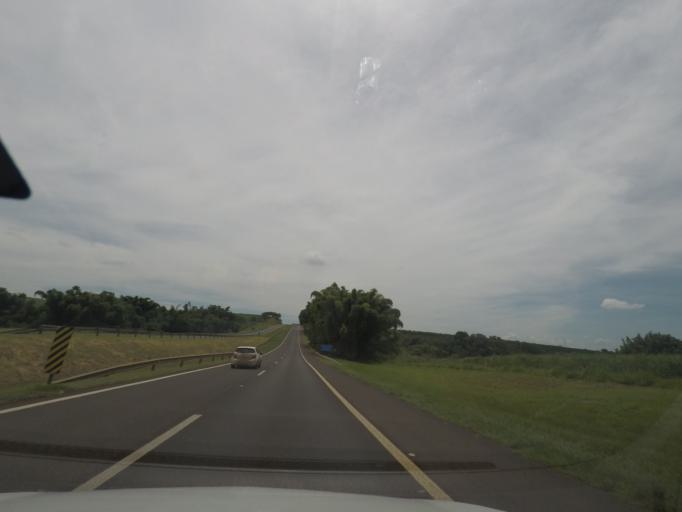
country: BR
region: Sao Paulo
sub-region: Bebedouro
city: Bebedouro
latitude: -21.0296
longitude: -48.4210
